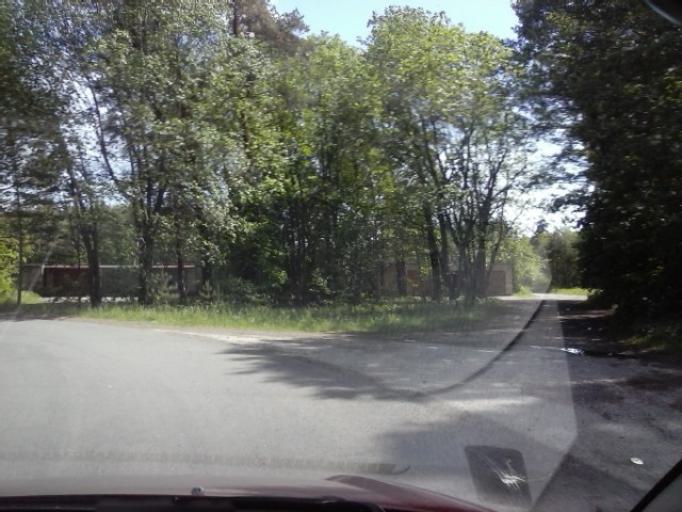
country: EE
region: Laeaene
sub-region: Haapsalu linn
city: Haapsalu
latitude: 58.9334
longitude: 23.5481
